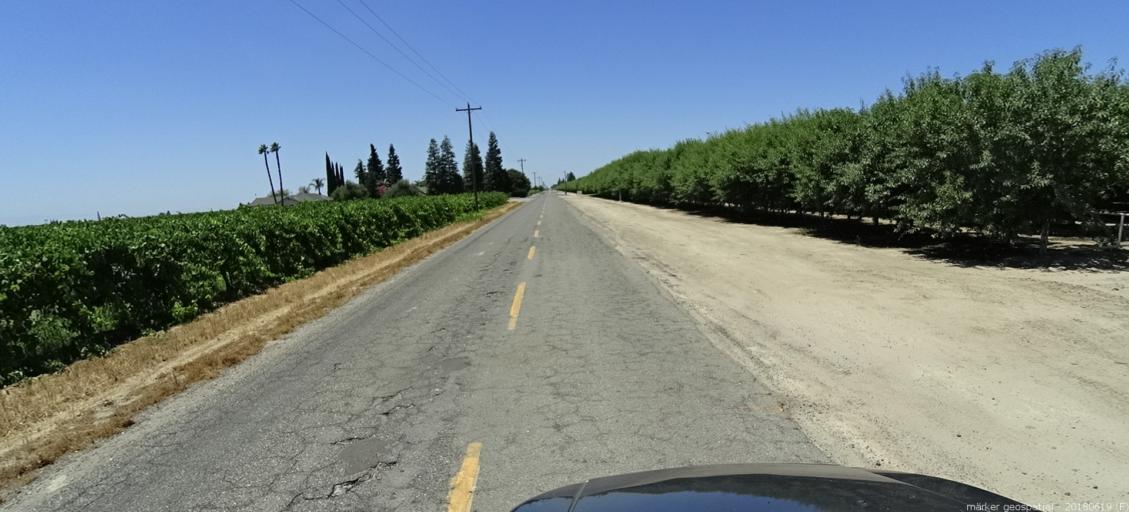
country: US
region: California
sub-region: Madera County
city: Parkwood
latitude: 36.8659
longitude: -120.0588
